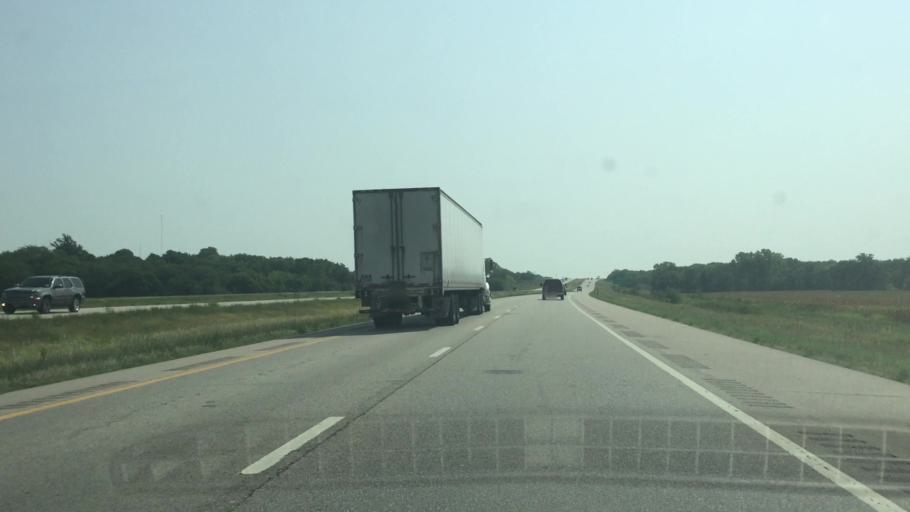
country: US
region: Kansas
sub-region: Lyon County
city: Emporia
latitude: 38.4111
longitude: -96.1115
